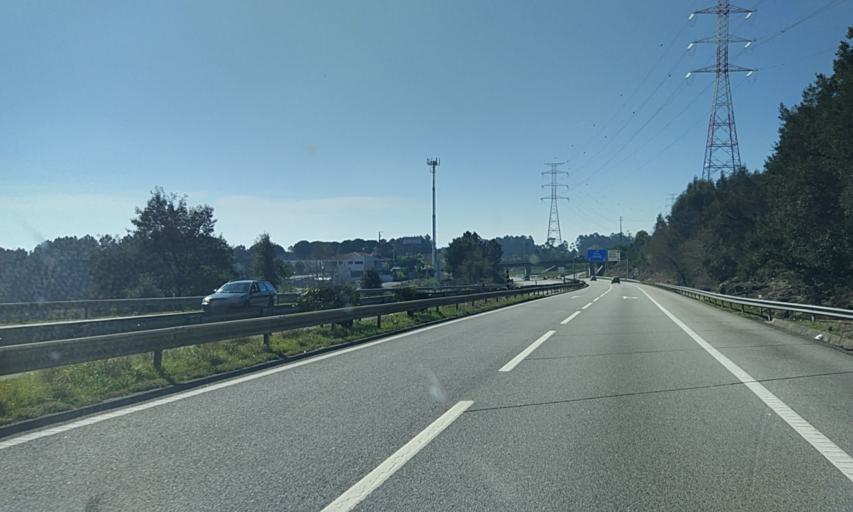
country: PT
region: Porto
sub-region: Paredes
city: Baltar
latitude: 41.1729
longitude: -8.3843
